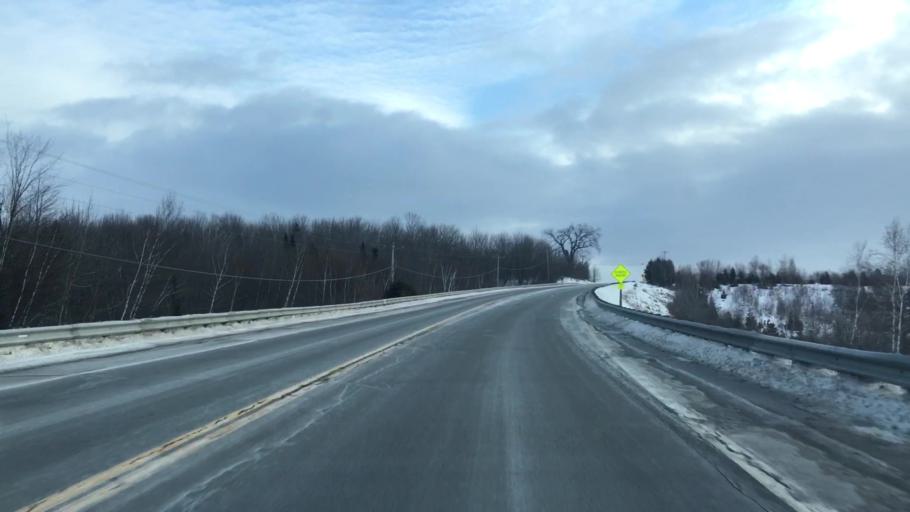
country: US
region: Maine
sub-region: Washington County
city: Calais
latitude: 45.0918
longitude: -67.4842
